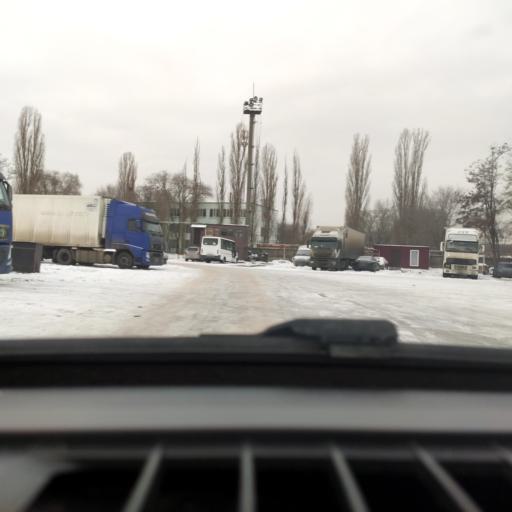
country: RU
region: Voronezj
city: Voronezh
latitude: 51.6698
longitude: 39.1364
